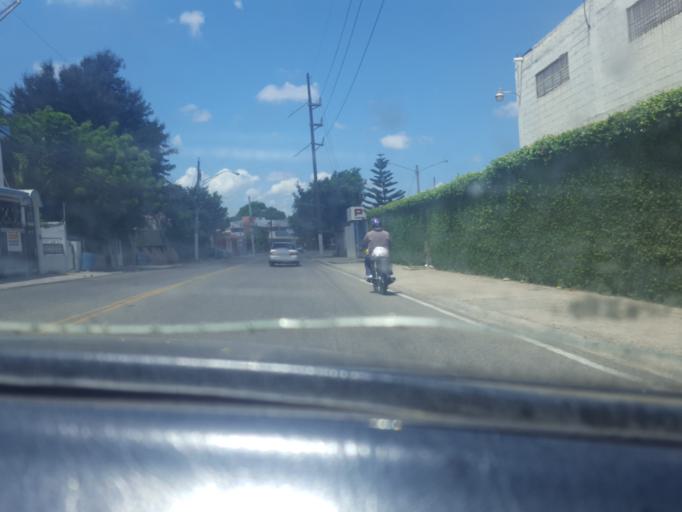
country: DO
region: Santiago
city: Santiago de los Caballeros
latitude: 19.4757
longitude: -70.7254
